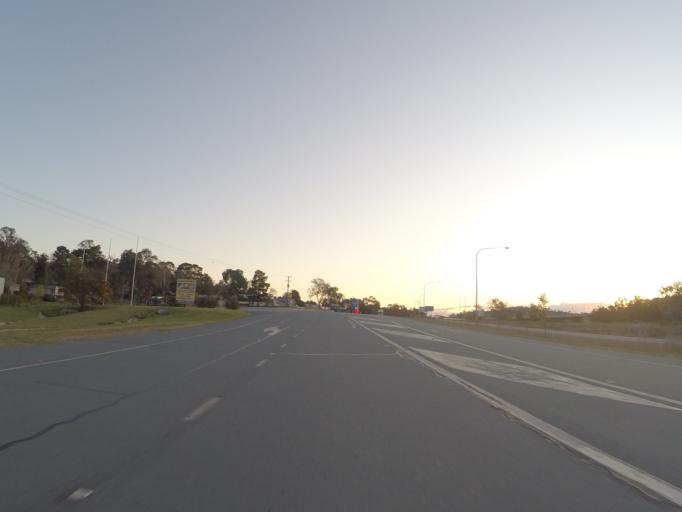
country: AU
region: Australian Capital Territory
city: Kaleen
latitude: -35.2015
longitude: 149.2130
